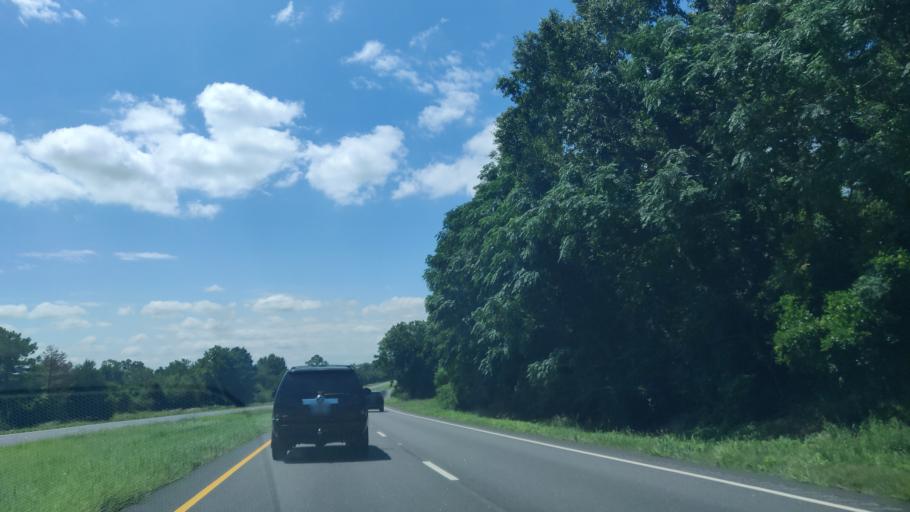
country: US
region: Georgia
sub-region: Stewart County
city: Richland
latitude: 32.1219
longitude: -84.6791
